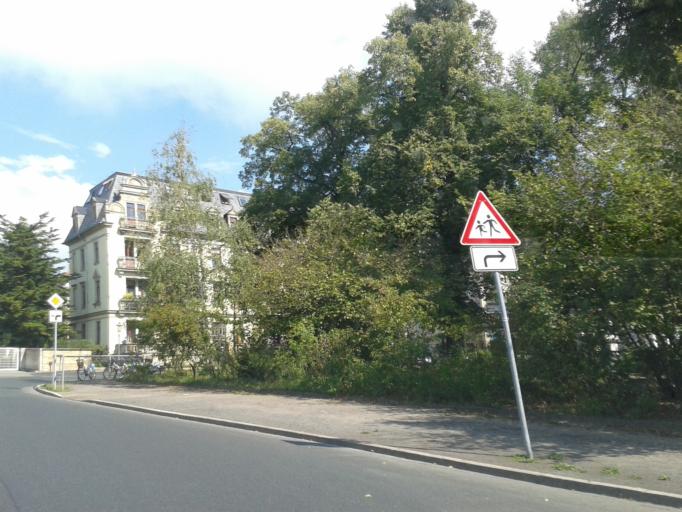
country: DE
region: Saxony
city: Albertstadt
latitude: 51.0486
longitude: 13.7935
